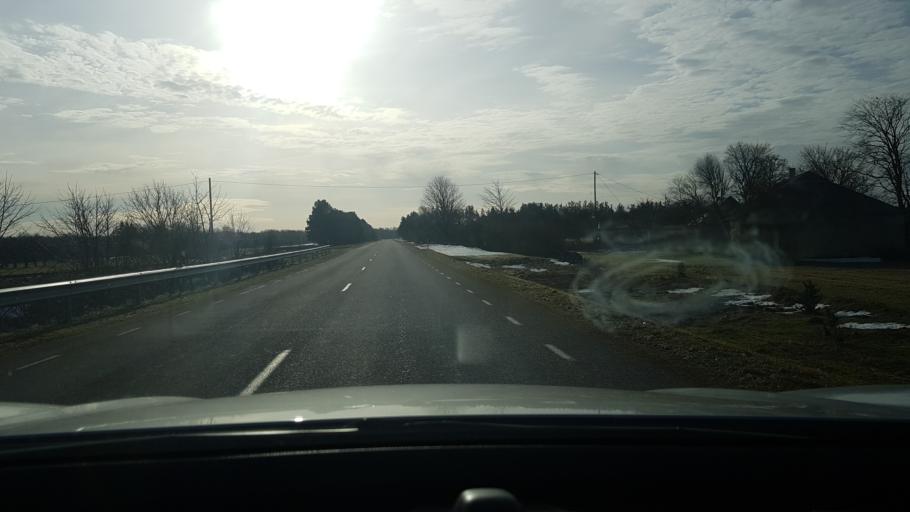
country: EE
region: Saare
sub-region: Kuressaare linn
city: Kuressaare
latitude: 58.5186
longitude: 22.7029
